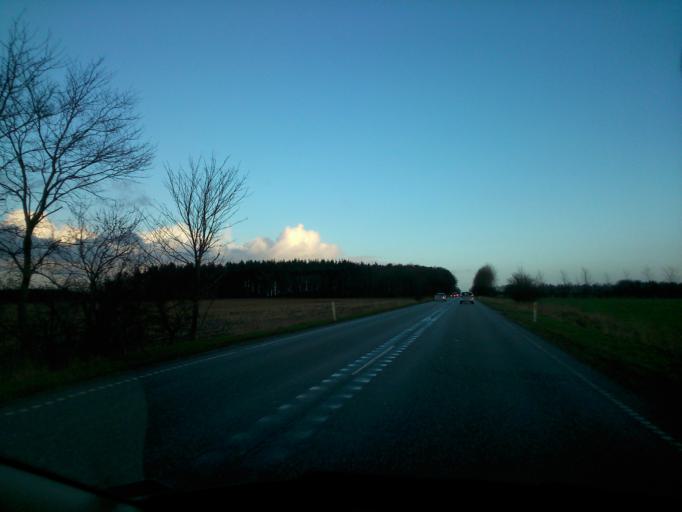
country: DK
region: Central Jutland
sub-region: Ringkobing-Skjern Kommune
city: Videbaek
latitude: 56.0971
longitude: 8.6798
